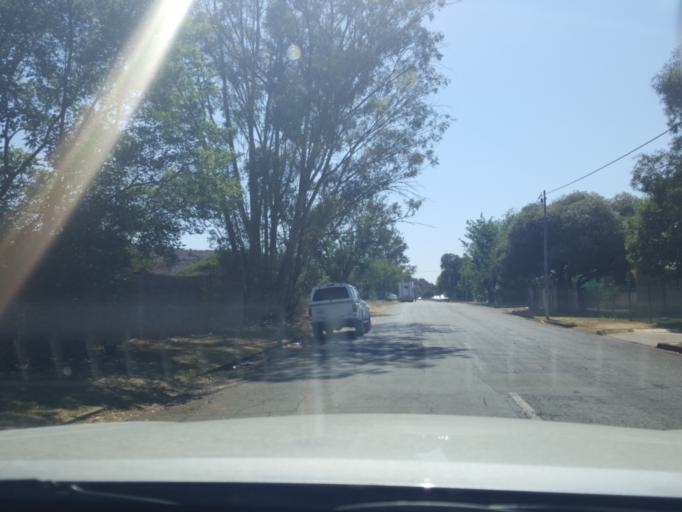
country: ZA
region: North-West
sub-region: Ngaka Modiri Molema District Municipality
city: Zeerust
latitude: -25.5430
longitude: 26.0797
